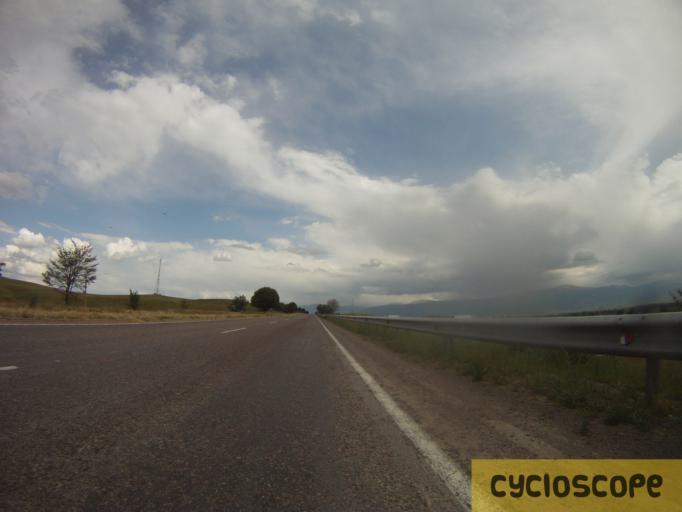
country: KZ
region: Almaty Oblysy
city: Burunday
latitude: 43.2515
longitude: 76.3217
